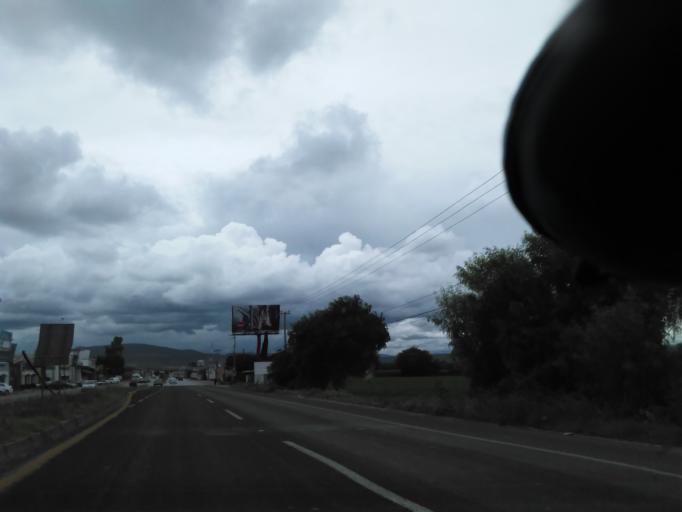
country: MX
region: Hidalgo
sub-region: Tula de Allende
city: Residencial Arboledas
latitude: 20.0579
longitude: -99.2948
